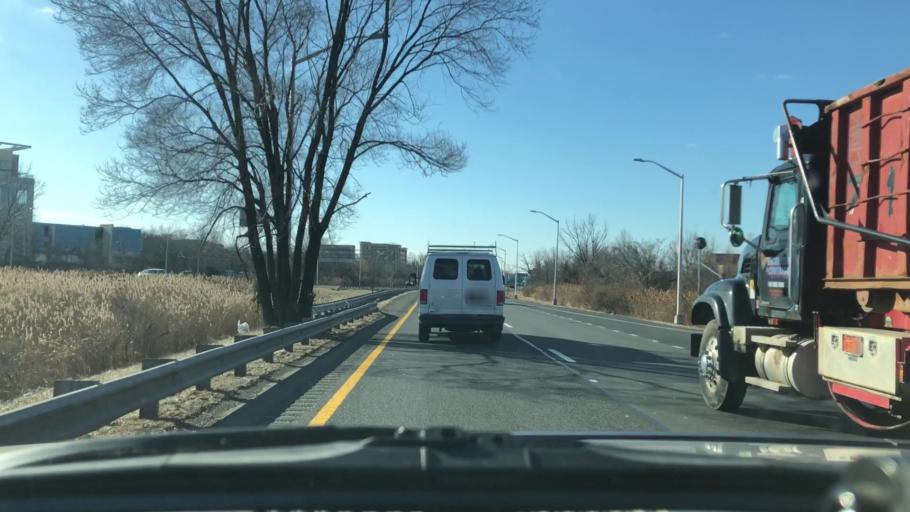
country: US
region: New York
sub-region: Richmond County
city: Bloomfield
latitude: 40.6175
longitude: -74.1777
